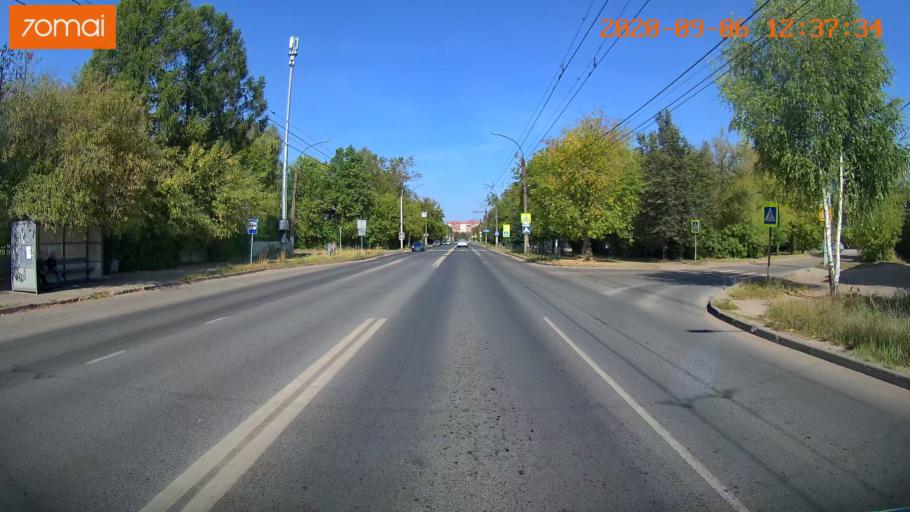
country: RU
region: Ivanovo
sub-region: Gorod Ivanovo
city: Ivanovo
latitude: 57.0280
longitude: 40.9801
